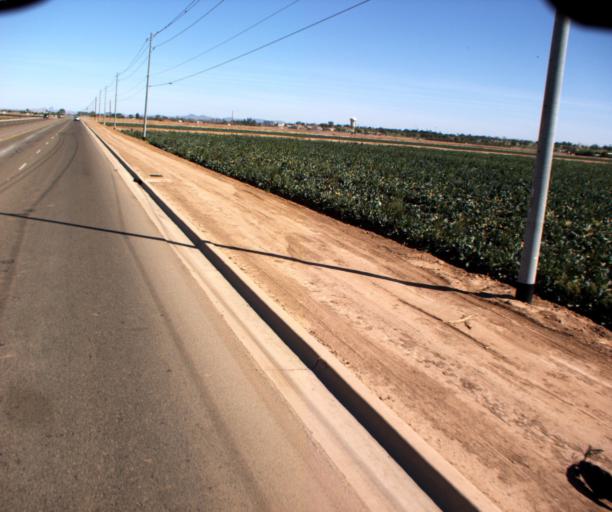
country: US
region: Arizona
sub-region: Yuma County
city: Somerton
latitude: 32.6444
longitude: -114.6500
